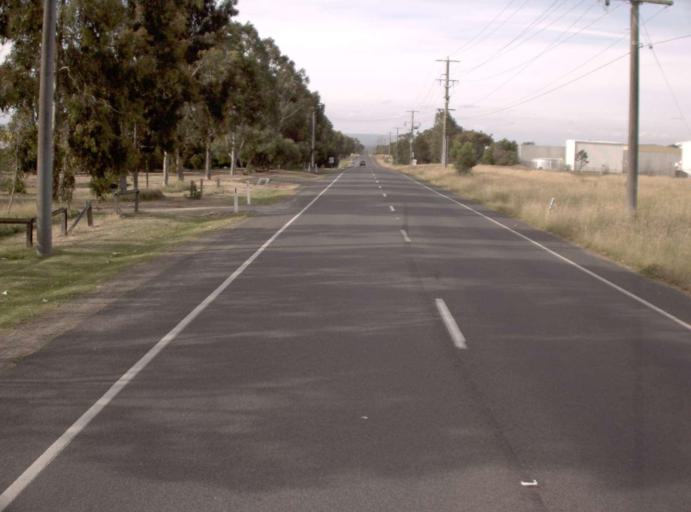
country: AU
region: Victoria
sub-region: Latrobe
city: Traralgon
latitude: -38.1878
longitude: 146.5611
